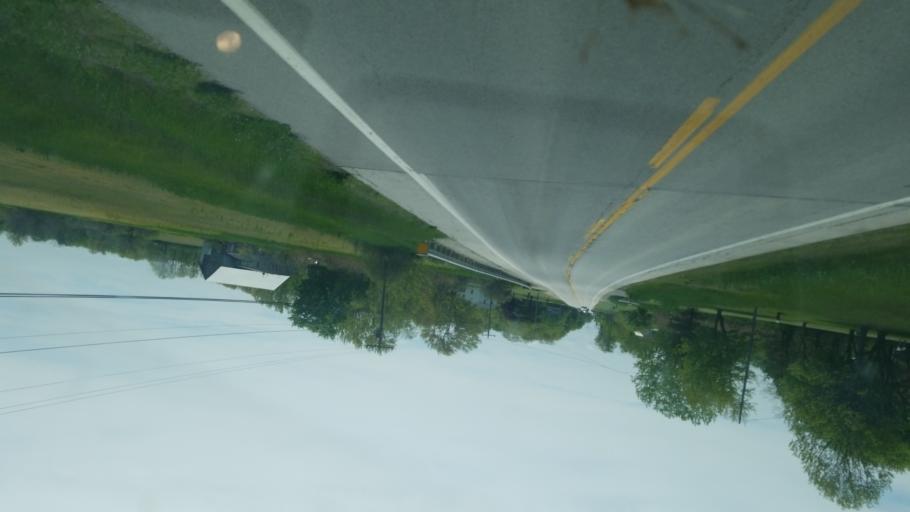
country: US
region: Ohio
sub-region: Ottawa County
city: Oak Harbor
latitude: 41.5565
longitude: -83.0708
